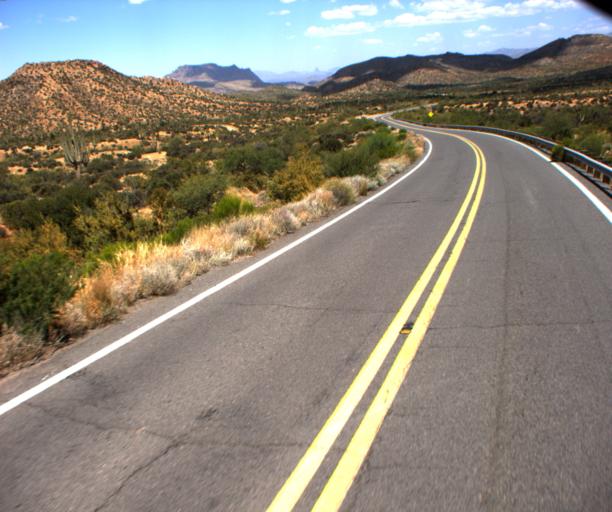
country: US
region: Arizona
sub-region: Pinal County
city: Superior
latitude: 33.2126
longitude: -111.0621
